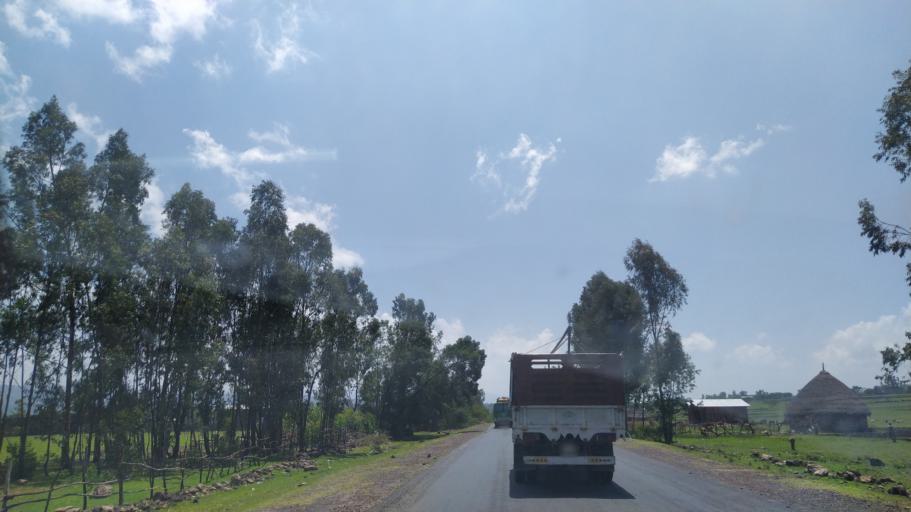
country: ET
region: Southern Nations, Nationalities, and People's Region
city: Butajira
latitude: 7.7699
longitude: 38.1379
